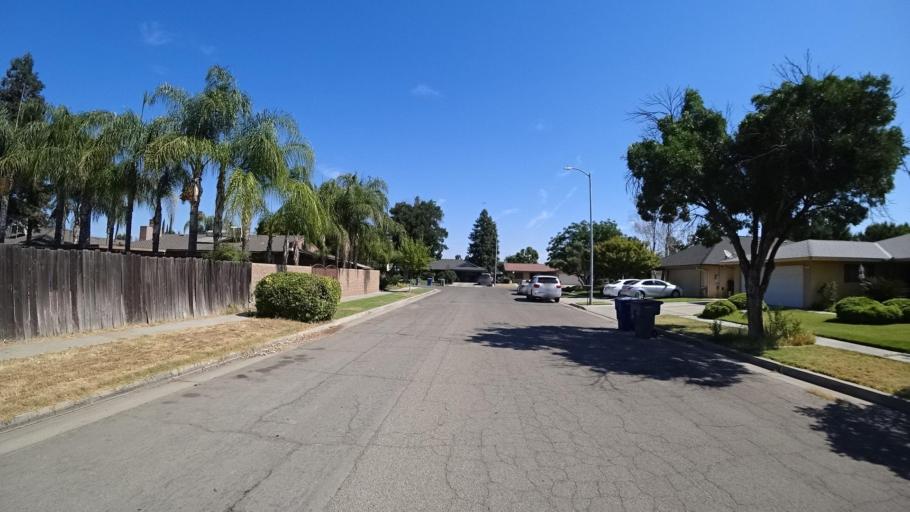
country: US
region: California
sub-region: Fresno County
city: Sunnyside
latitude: 36.7484
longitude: -119.6841
